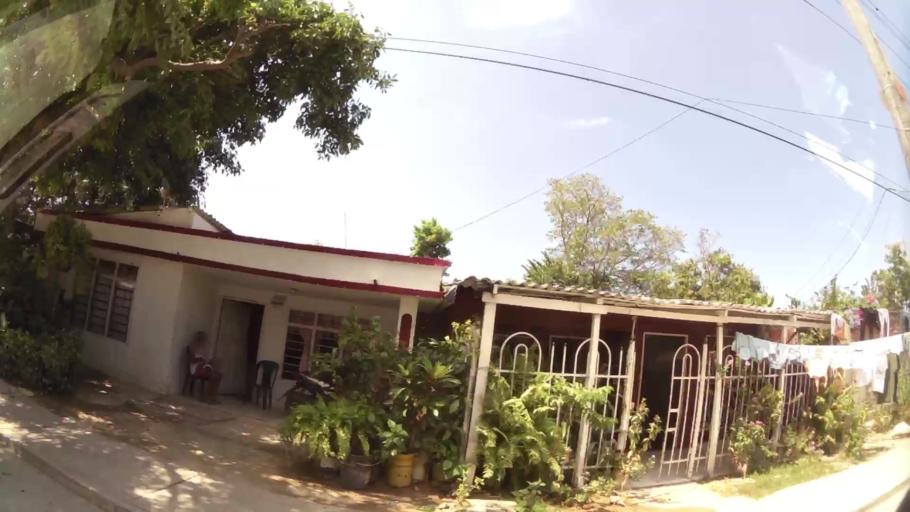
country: CO
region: Bolivar
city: Cartagena
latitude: 10.3694
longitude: -75.5073
